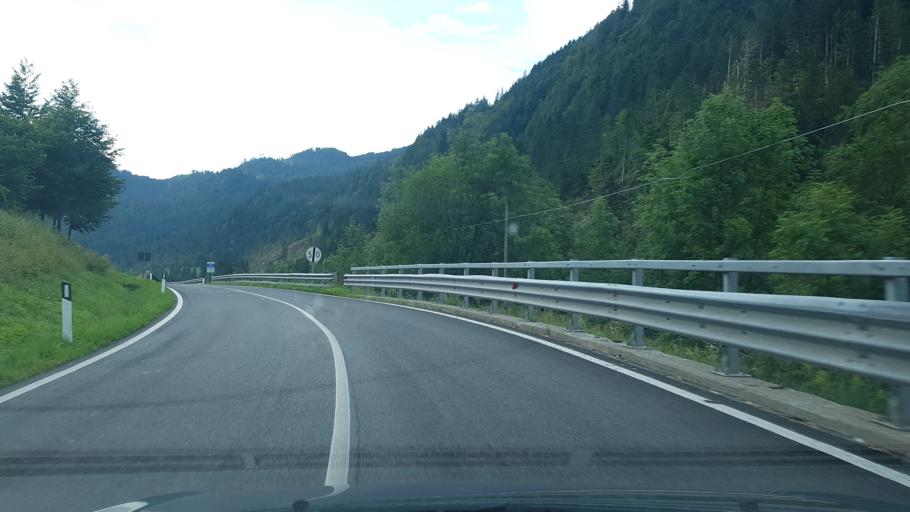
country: IT
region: Friuli Venezia Giulia
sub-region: Provincia di Udine
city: Forni Avoltri
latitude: 46.5824
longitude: 12.7831
